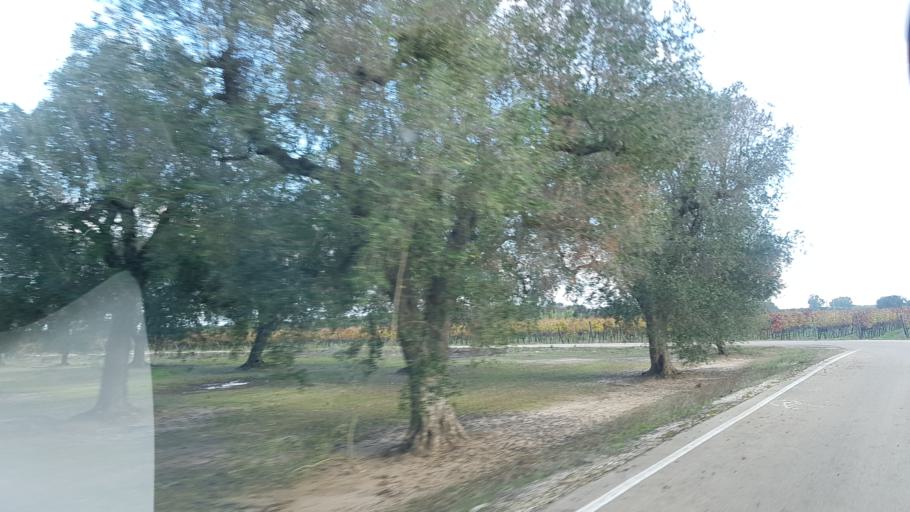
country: IT
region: Apulia
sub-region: Provincia di Brindisi
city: San Pietro Vernotico
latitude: 40.5118
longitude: 18.0172
